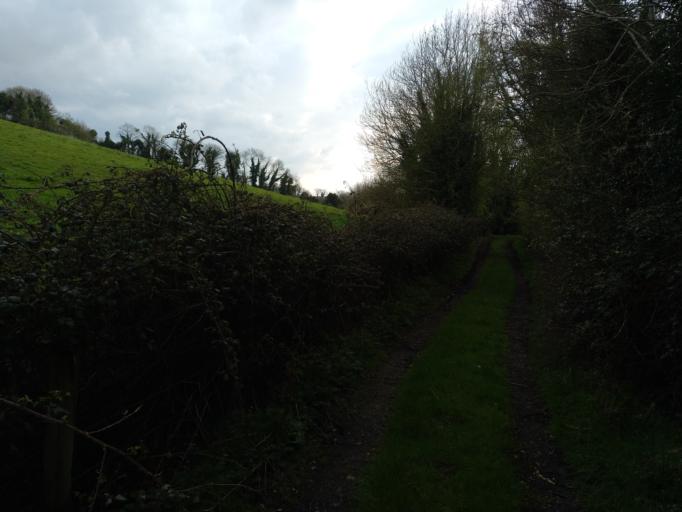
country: IE
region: Ulster
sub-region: County Monaghan
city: Clones
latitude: 54.1939
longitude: -7.1509
